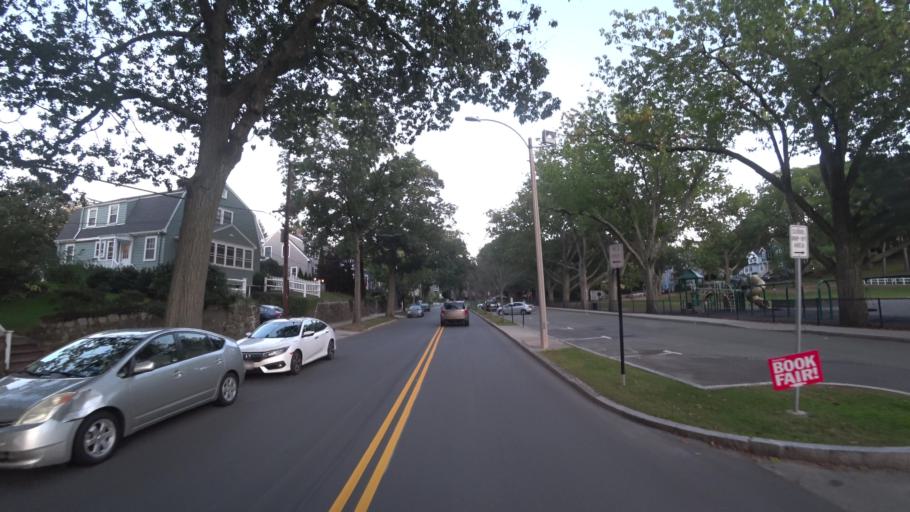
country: US
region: Massachusetts
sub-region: Norfolk County
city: Brookline
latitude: 42.3283
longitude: -71.1476
